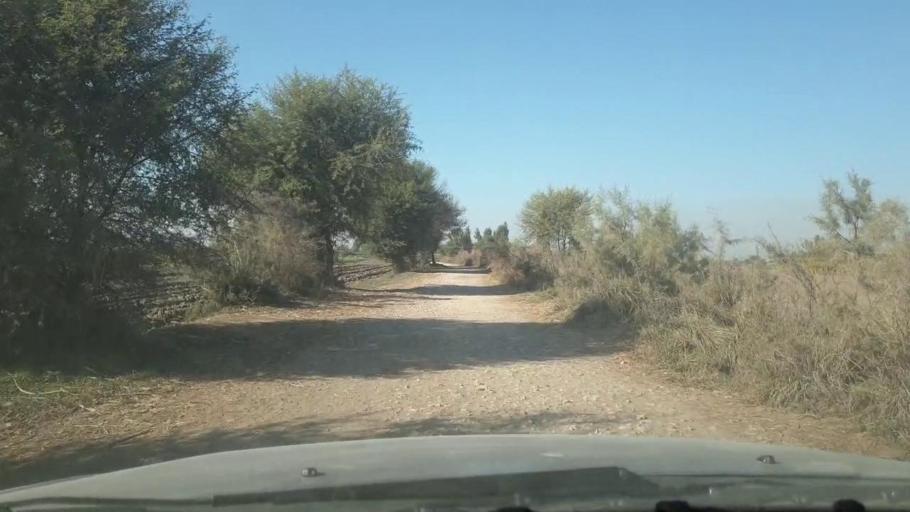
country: PK
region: Sindh
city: Pano Aqil
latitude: 27.9765
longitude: 69.1716
